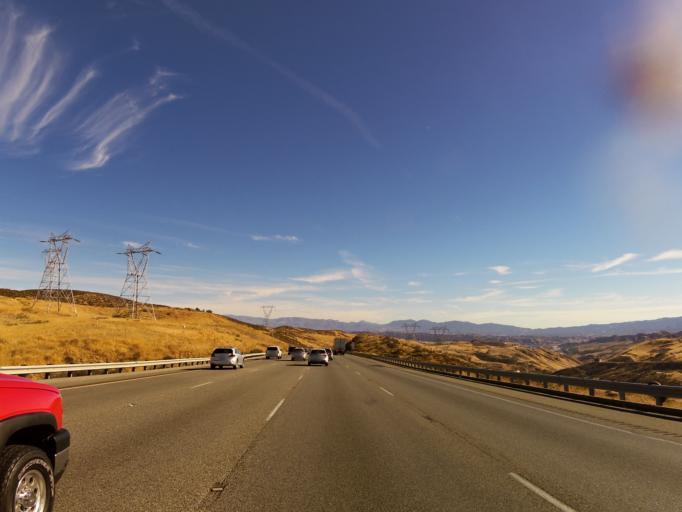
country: US
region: California
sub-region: Los Angeles County
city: Castaic
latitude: 34.5474
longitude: -118.6596
